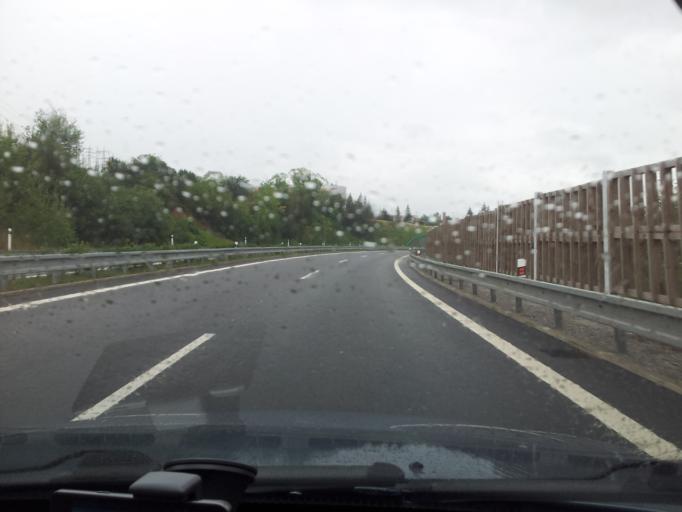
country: SK
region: Banskobystricky
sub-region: Okres Banska Bystrica
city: Banska Bystrica
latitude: 48.7431
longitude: 19.1761
